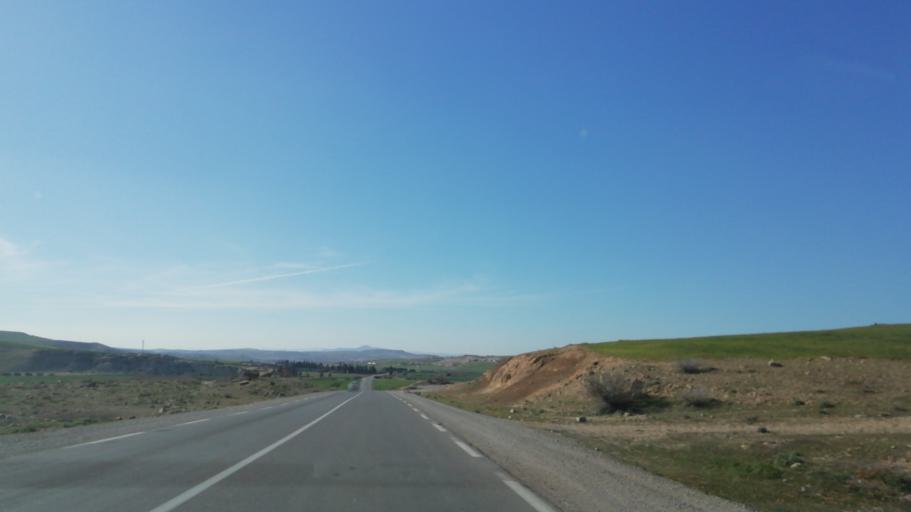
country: DZ
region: Mascara
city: Oued el Abtal
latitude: 35.4552
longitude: 0.7655
